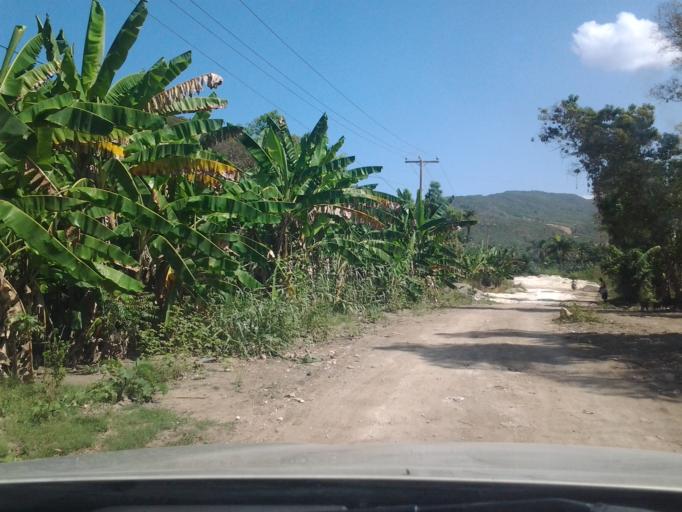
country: HT
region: Ouest
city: Tigwav
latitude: 18.4405
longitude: -72.8442
